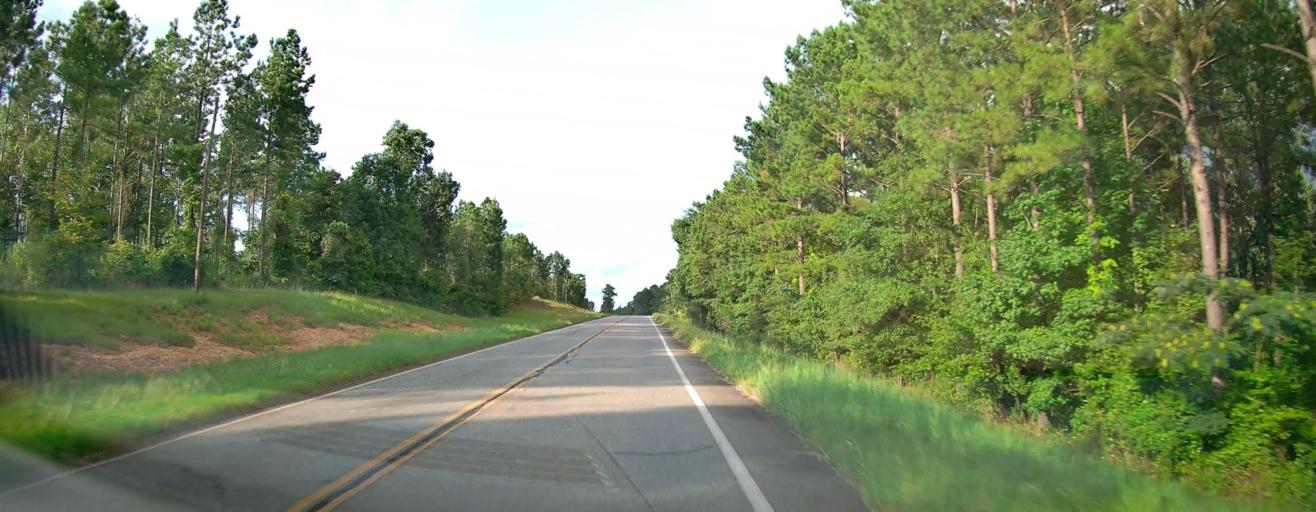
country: US
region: Georgia
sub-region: Crawford County
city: Roberta
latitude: 32.8100
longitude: -84.0282
